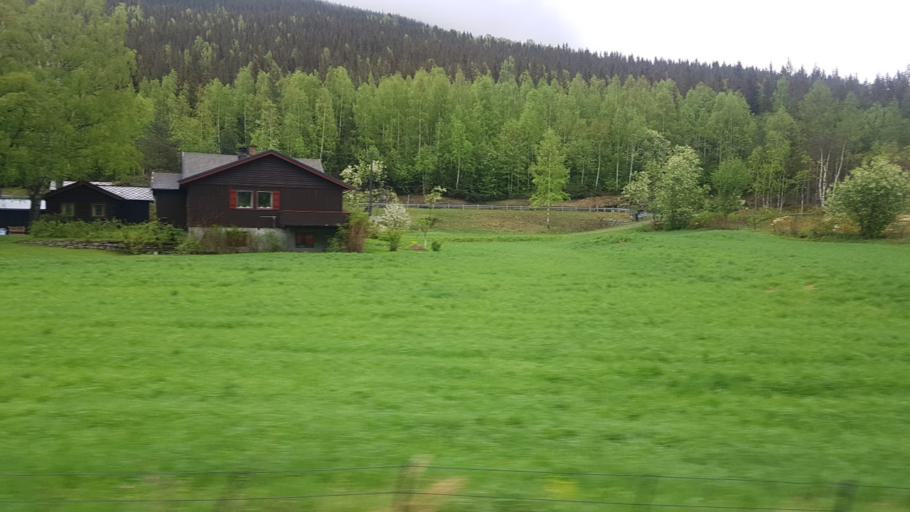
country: NO
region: Oppland
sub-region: Nord-Fron
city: Vinstra
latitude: 61.6200
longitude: 9.7120
